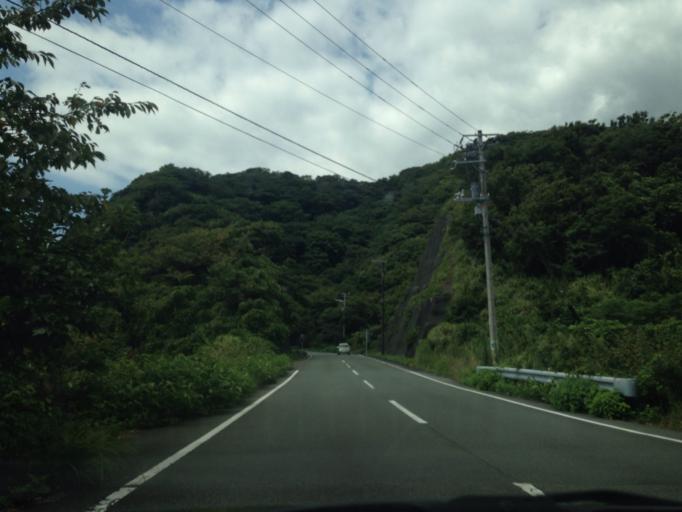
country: JP
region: Shizuoka
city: Shimoda
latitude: 34.6632
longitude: 138.7930
